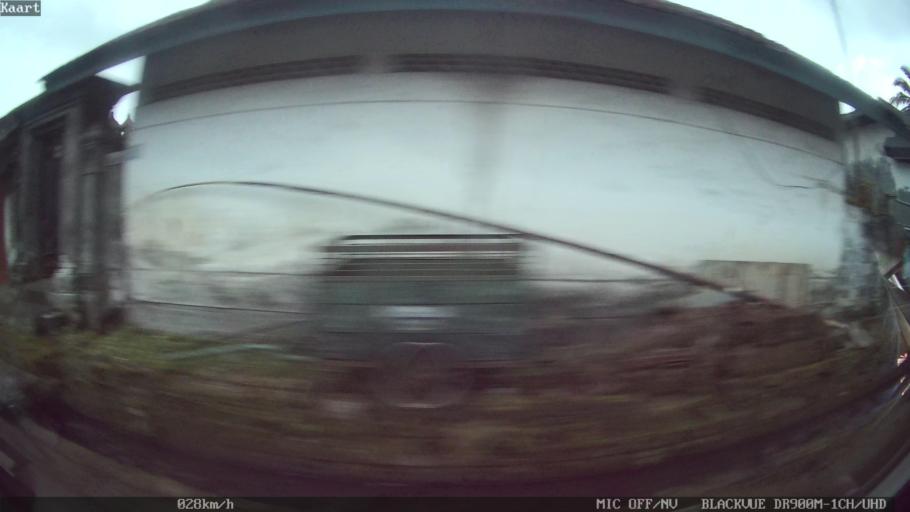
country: ID
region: Bali
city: Tegalalang
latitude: -8.4481
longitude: 115.2750
